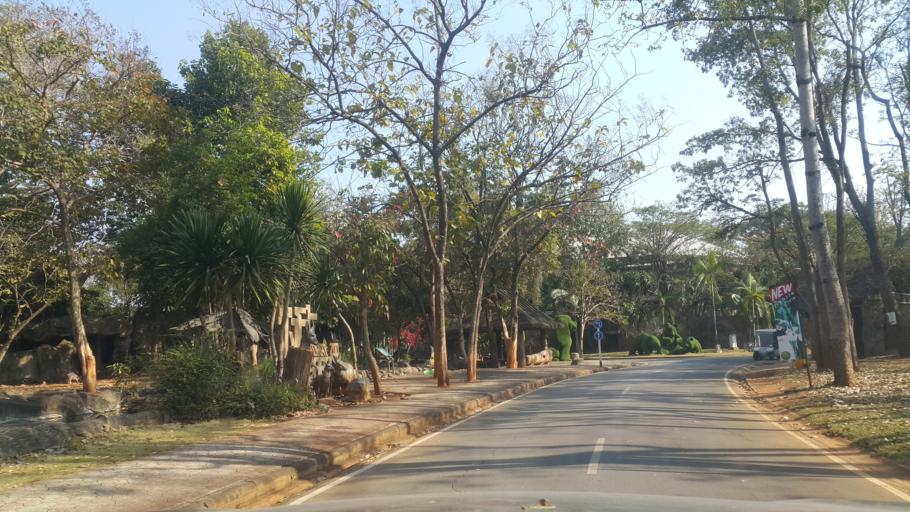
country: TH
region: Nakhon Ratchasima
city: Nakhon Ratchasima
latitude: 14.8529
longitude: 102.0842
